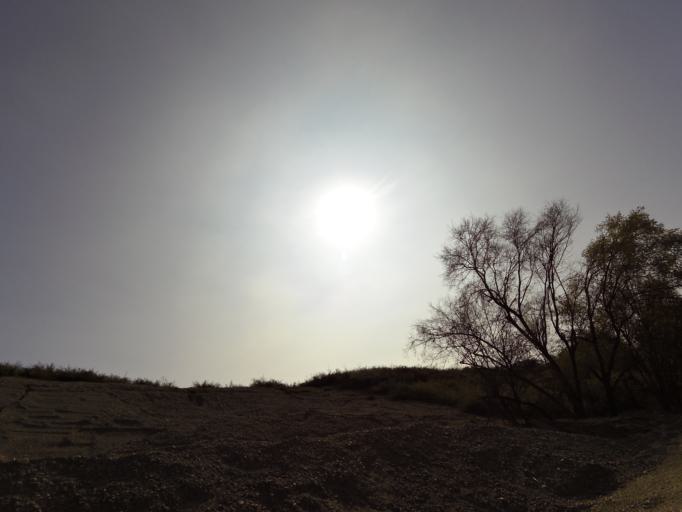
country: IT
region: Lombardy
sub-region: Citta metropolitana di Milano
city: Chiaravalle
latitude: 45.4288
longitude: 9.2358
